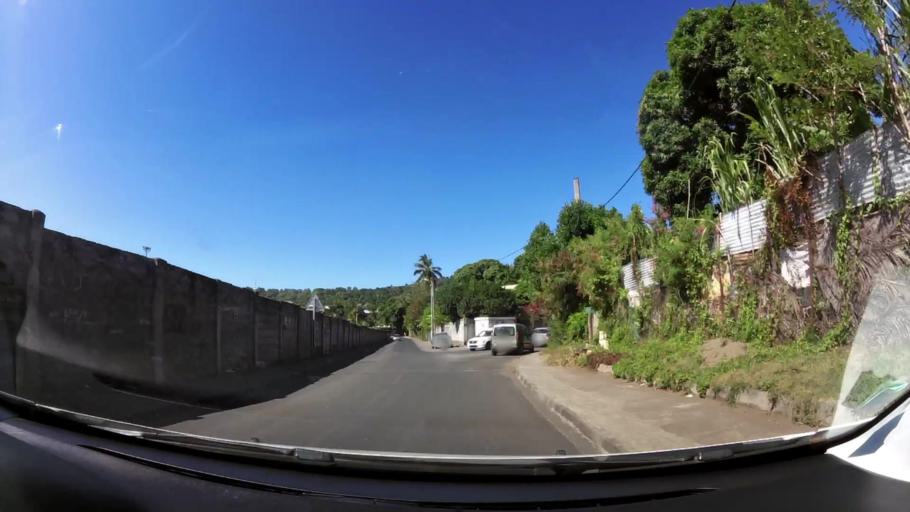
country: YT
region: Pamandzi
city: Pamandzi
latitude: -12.7890
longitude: 45.2764
